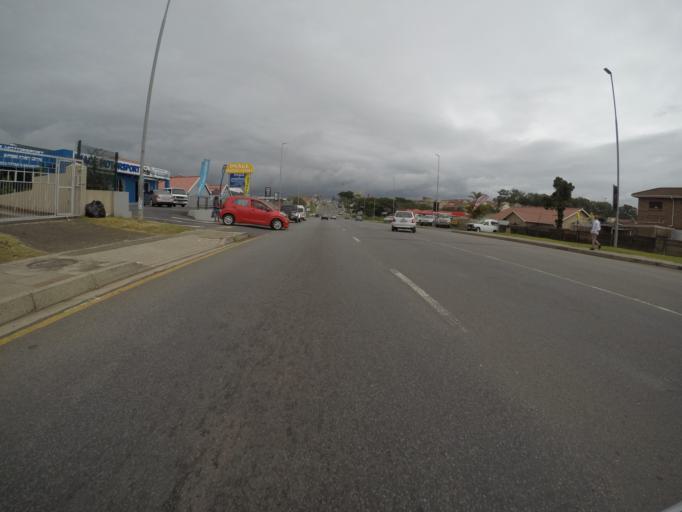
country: ZA
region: Eastern Cape
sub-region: Buffalo City Metropolitan Municipality
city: East London
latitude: -32.9949
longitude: 27.8706
